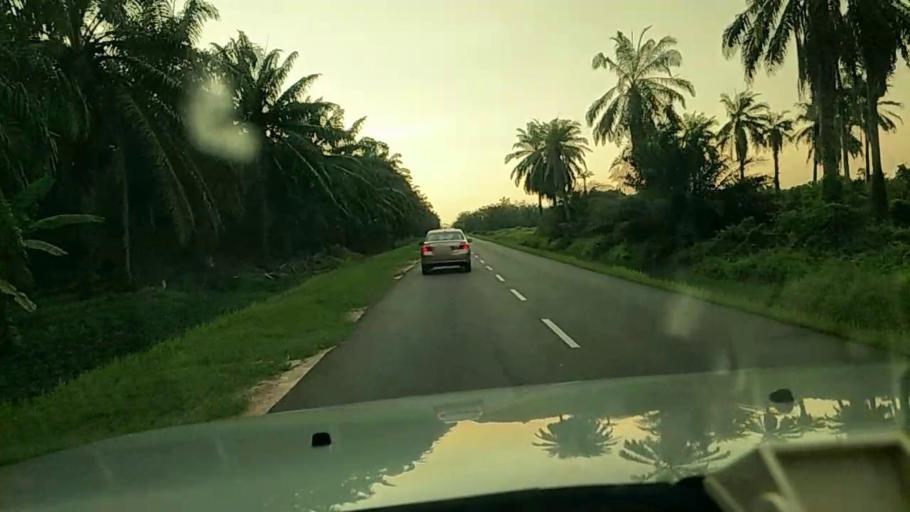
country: MY
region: Selangor
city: Kuala Selangor
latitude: 3.3173
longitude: 101.2801
